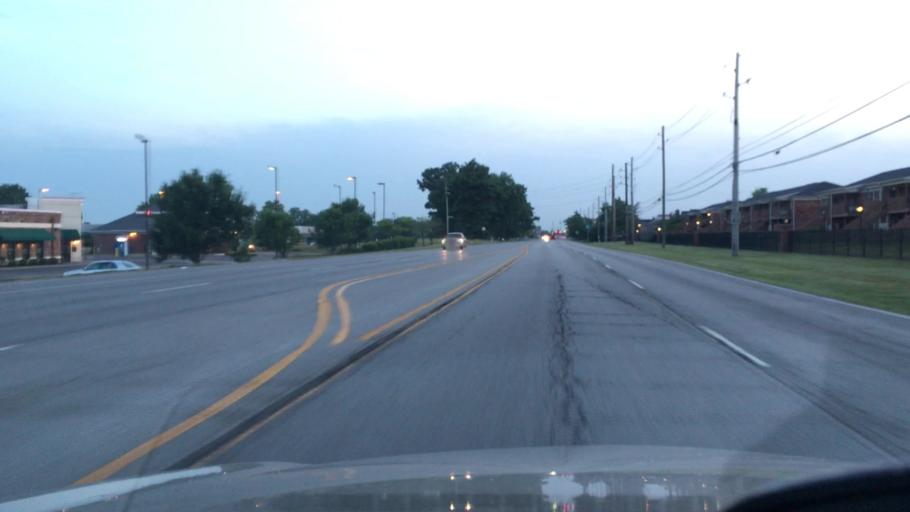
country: US
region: Indiana
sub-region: Marion County
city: Lawrence
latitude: 39.8929
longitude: -86.0461
